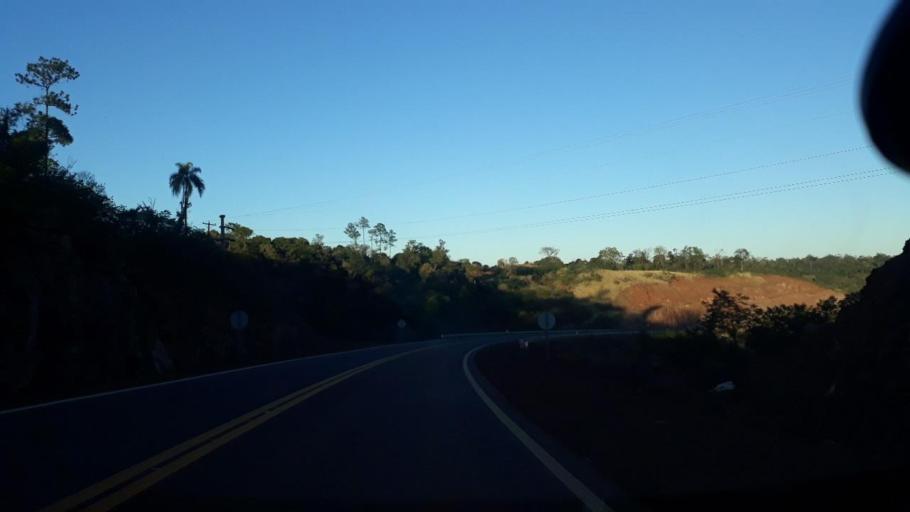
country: AR
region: Misiones
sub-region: Departamento de San Pedro
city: San Pedro
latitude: -26.5382
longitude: -53.9415
